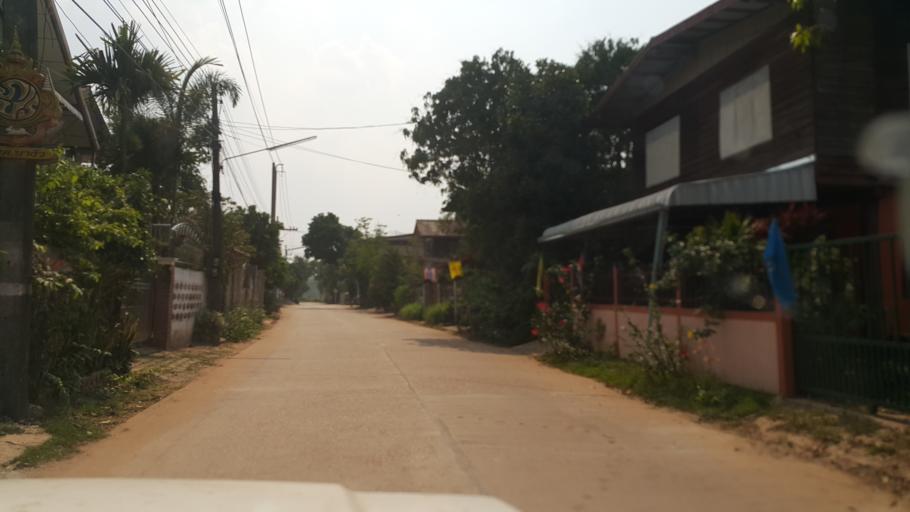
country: TH
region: Nakhon Phanom
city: Ban Phaeng
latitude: 17.9622
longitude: 104.1928
